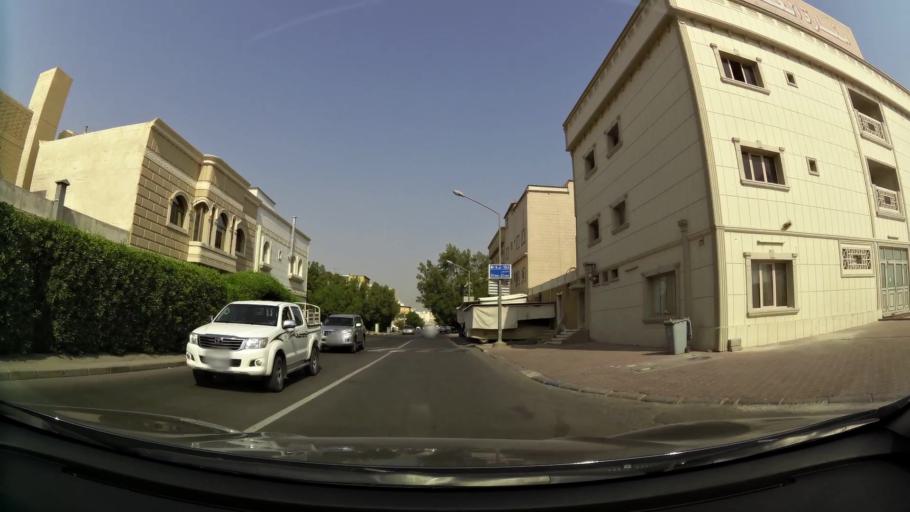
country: KW
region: Al Asimah
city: Ar Rabiyah
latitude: 29.2845
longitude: 47.8937
